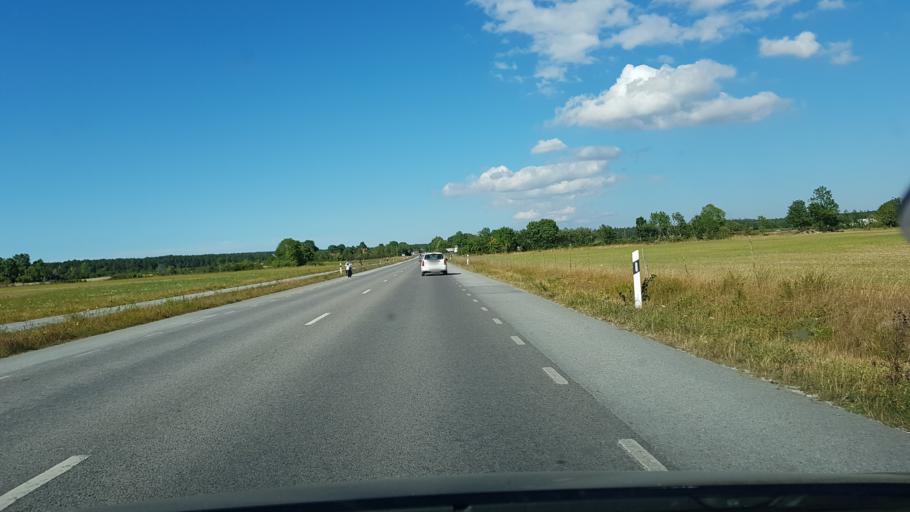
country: SE
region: Gotland
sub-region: Gotland
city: Vibble
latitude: 57.5218
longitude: 18.1664
